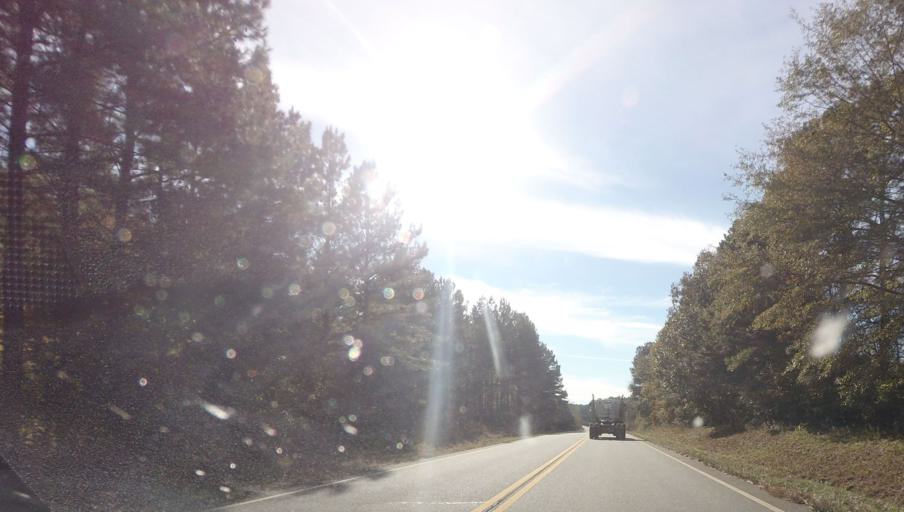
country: US
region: Georgia
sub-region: Talbot County
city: Talbotton
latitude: 32.7040
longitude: -84.4082
